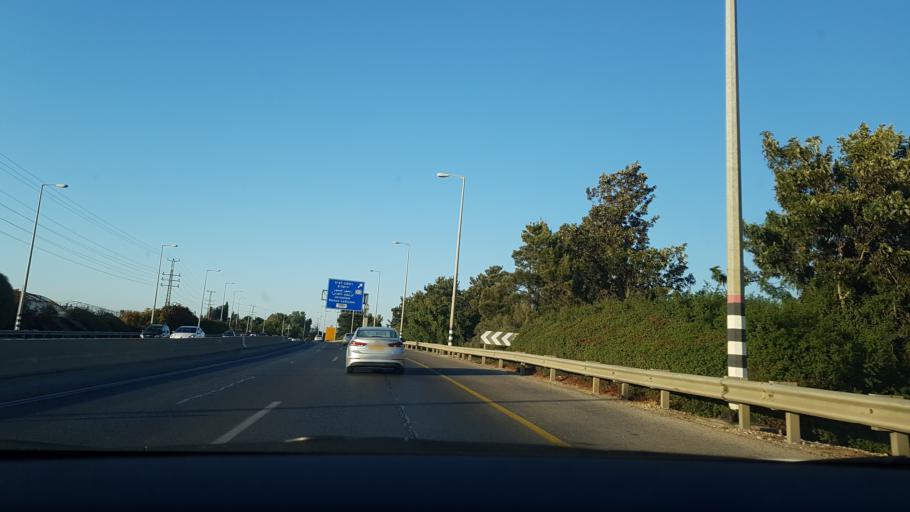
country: IL
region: Central District
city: Ness Ziona
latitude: 31.9392
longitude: 34.7797
